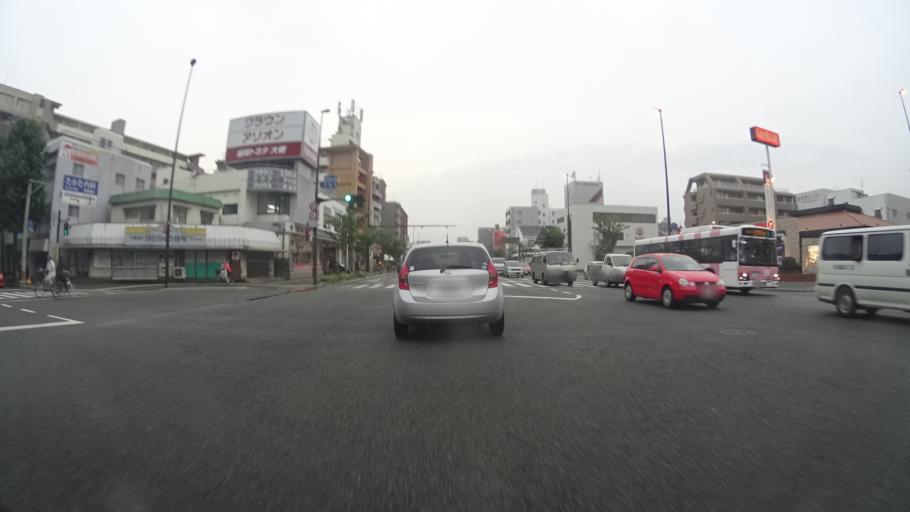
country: JP
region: Fukuoka
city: Fukuoka-shi
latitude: 33.5635
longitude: 130.4235
